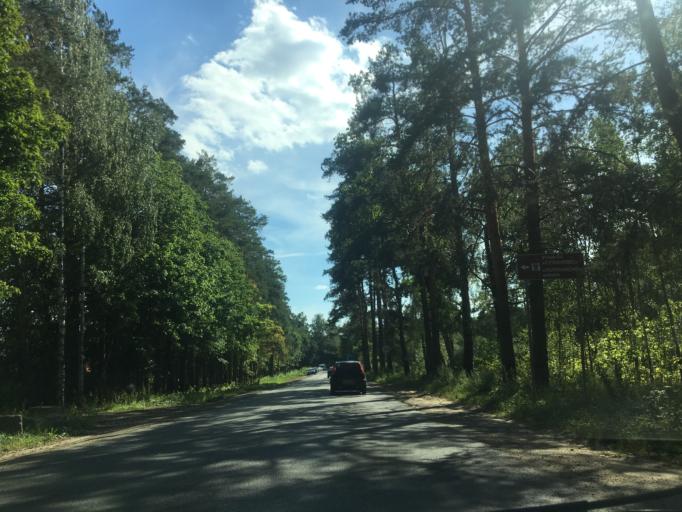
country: RU
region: Moscow
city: Zagor'ye
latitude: 55.5298
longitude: 37.6637
